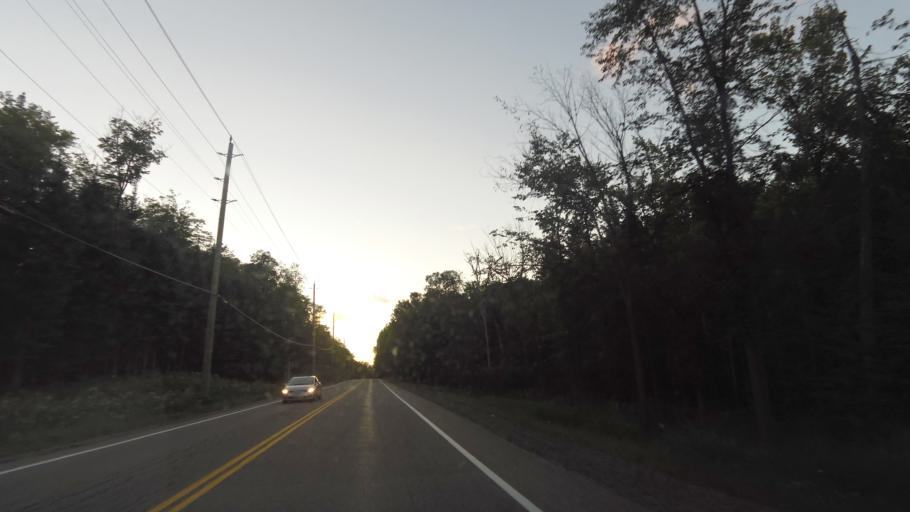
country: CA
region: Ontario
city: Bancroft
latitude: 45.0299
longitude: -78.4051
